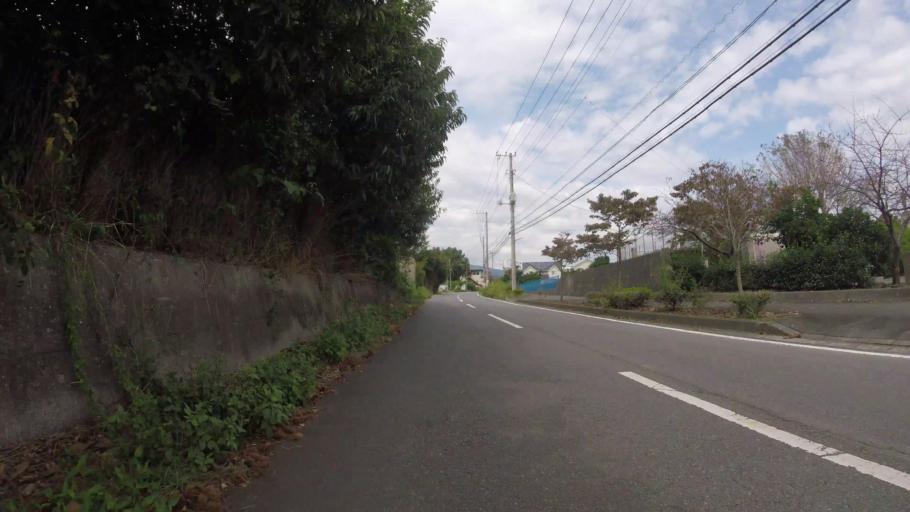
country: JP
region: Shizuoka
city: Numazu
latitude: 35.1347
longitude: 138.8582
